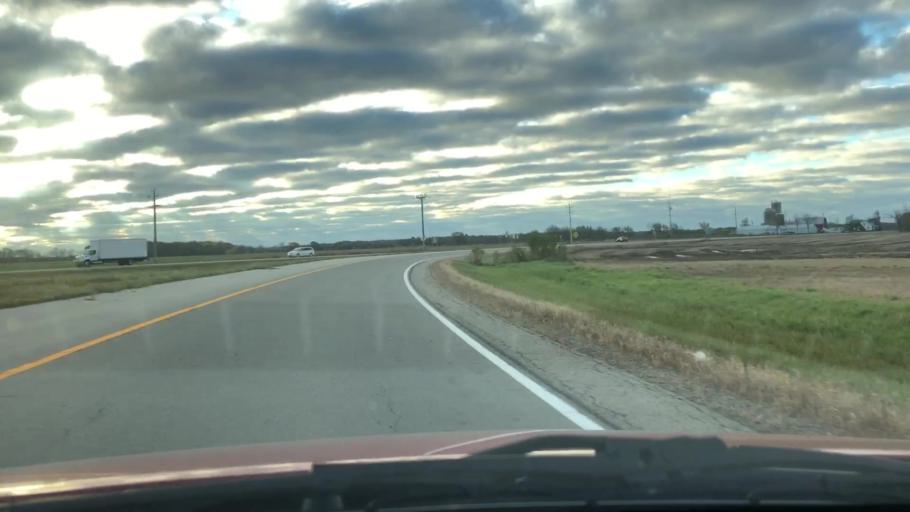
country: US
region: Wisconsin
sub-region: Outagamie County
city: Seymour
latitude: 44.4994
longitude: -88.2928
